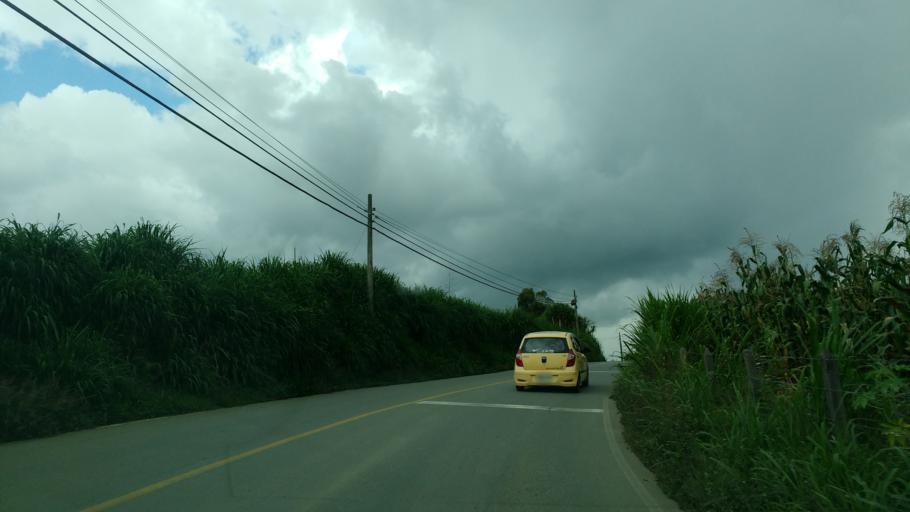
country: CO
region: Antioquia
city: Marinilla
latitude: 6.1805
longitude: -75.3038
